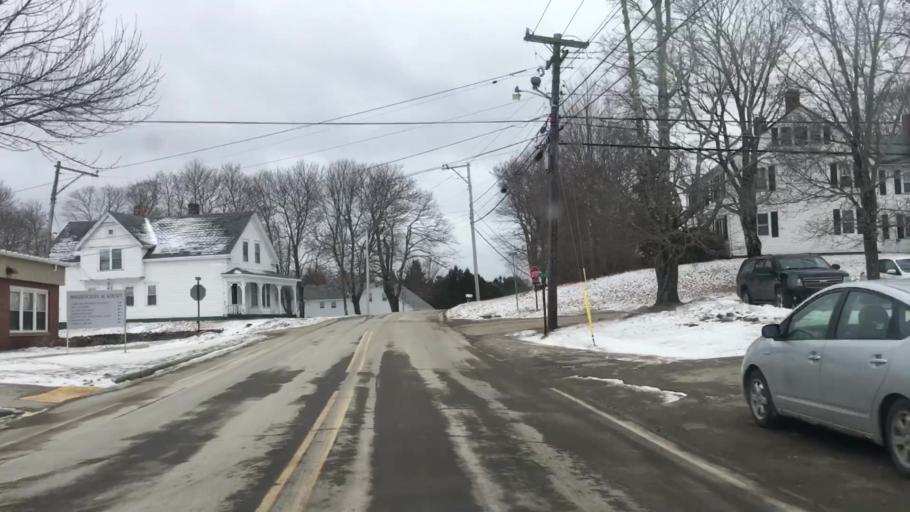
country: US
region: Maine
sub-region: Washington County
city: East Machias
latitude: 44.7343
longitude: -67.3892
